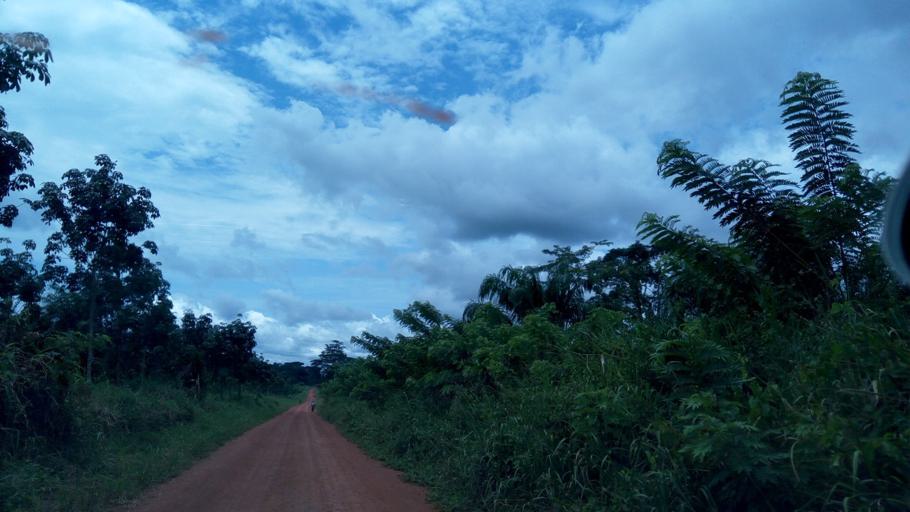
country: CD
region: Equateur
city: Gemena
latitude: 2.4975
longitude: 20.0901
